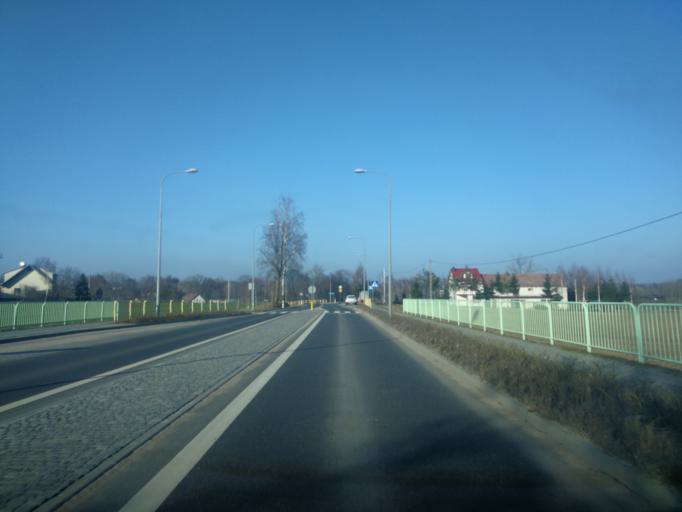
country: PL
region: Warmian-Masurian Voivodeship
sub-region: Powiat ilawski
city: Lubawa
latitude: 53.4536
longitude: 19.7786
